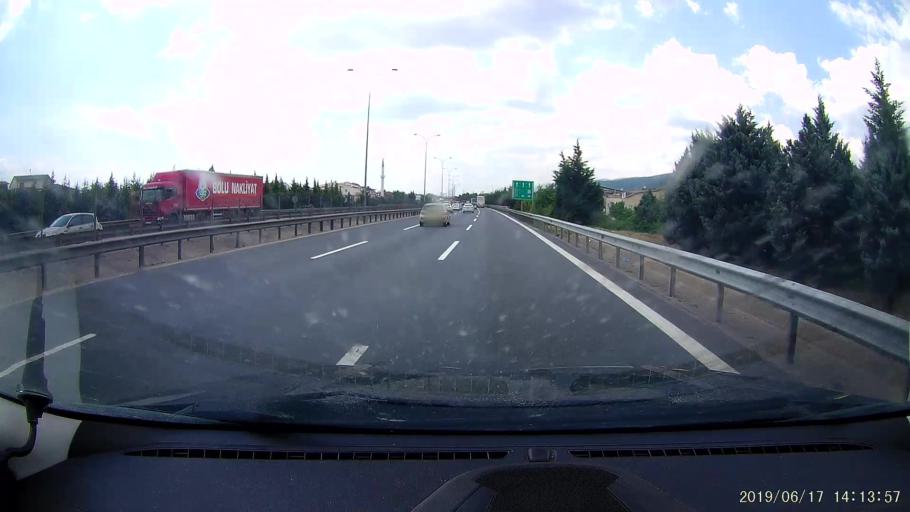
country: TR
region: Kocaeli
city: Korfez
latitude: 40.7699
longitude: 29.7936
